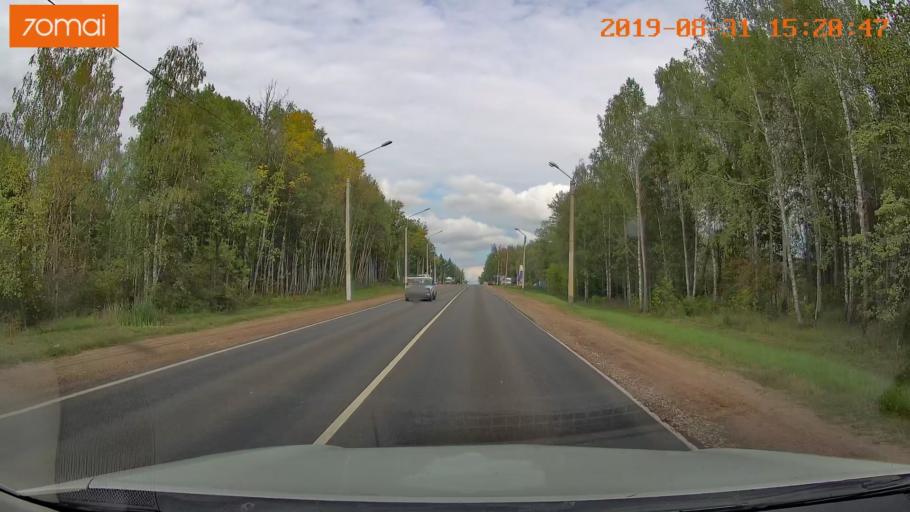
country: RU
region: Kaluga
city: Baryatino
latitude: 54.4922
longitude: 34.4422
